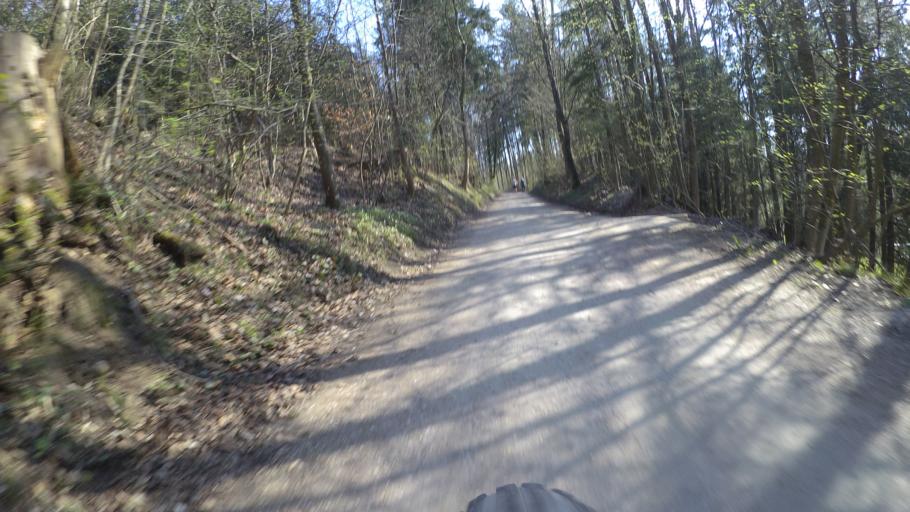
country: DE
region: Bavaria
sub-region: Upper Bavaria
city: Traunreut
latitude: 47.9514
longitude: 12.5886
